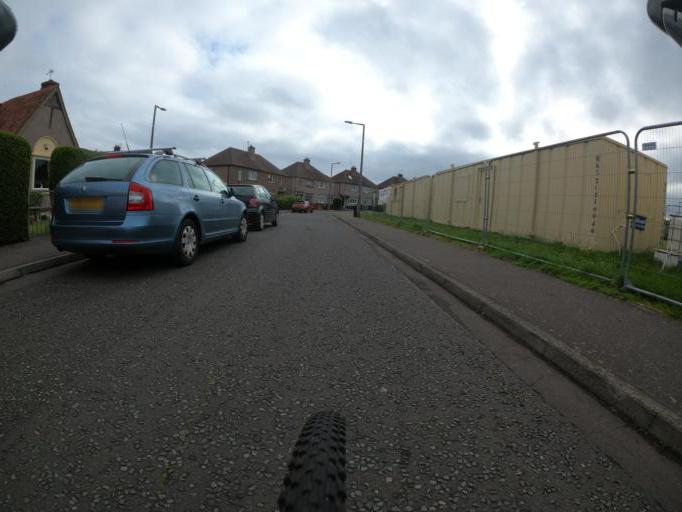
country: GB
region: Scotland
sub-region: Edinburgh
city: Edinburgh
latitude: 55.9657
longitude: -3.2474
